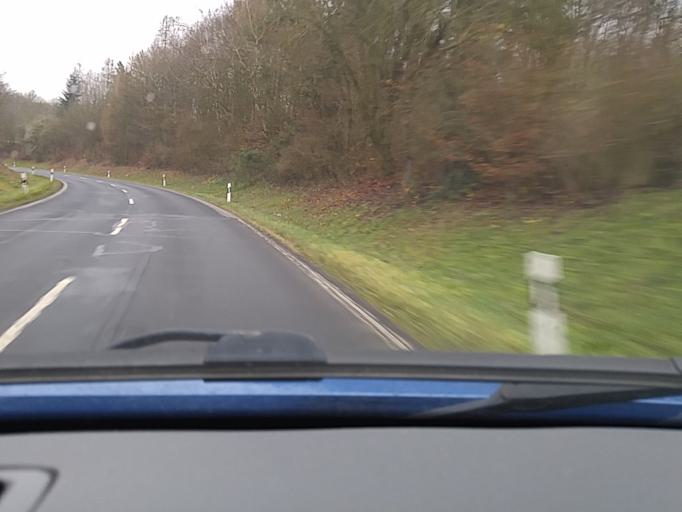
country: DE
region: Hesse
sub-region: Regierungsbezirk Darmstadt
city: Ranstadt
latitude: 50.3600
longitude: 8.9333
